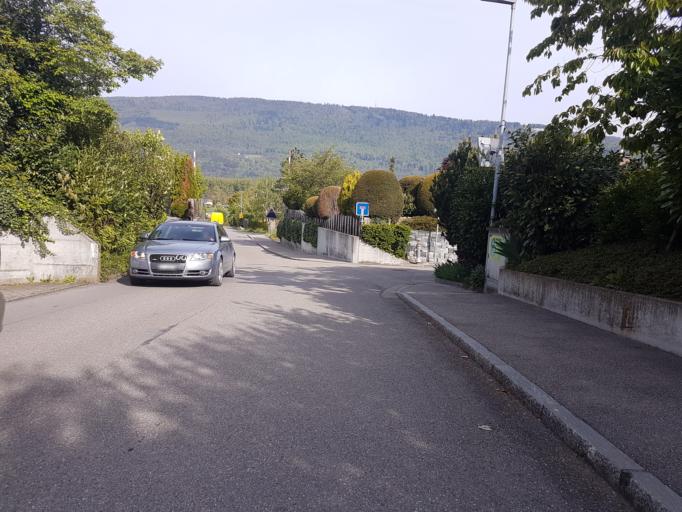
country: CH
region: Bern
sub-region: Biel/Bienne District
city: Nidau
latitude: 47.1133
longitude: 7.2307
